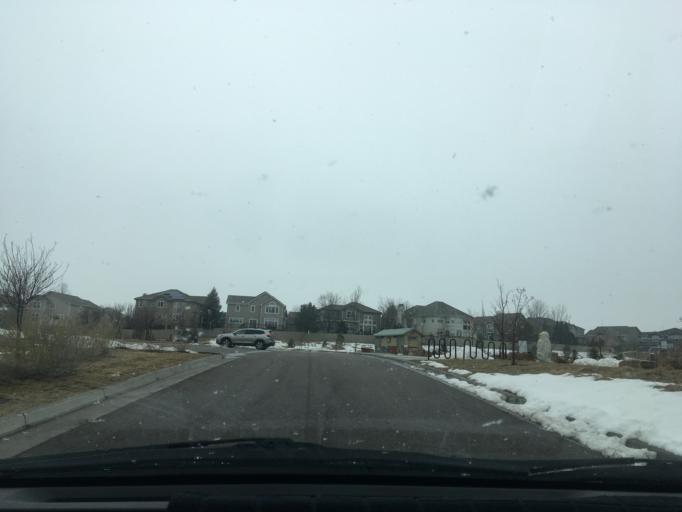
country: US
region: Colorado
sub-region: Boulder County
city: Superior
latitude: 39.9230
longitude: -105.1612
